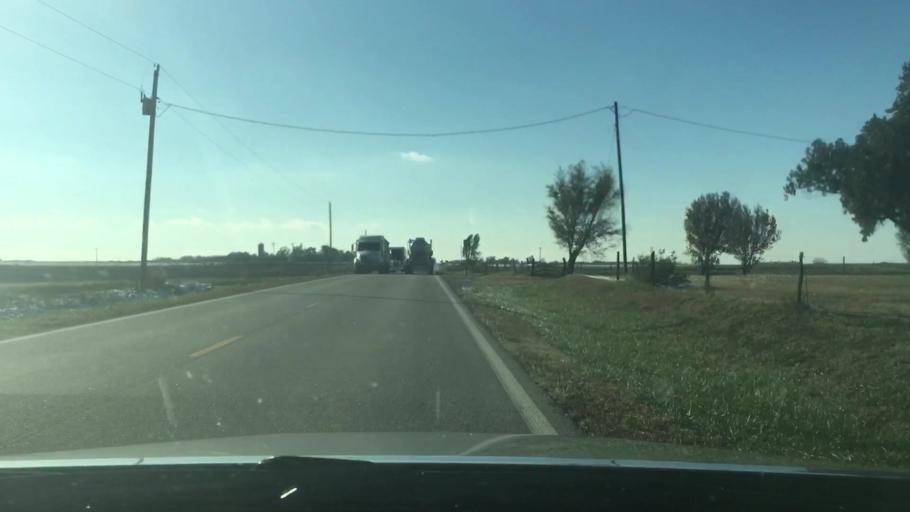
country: US
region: Kansas
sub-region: Rice County
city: Sterling
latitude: 38.1447
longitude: -98.1746
